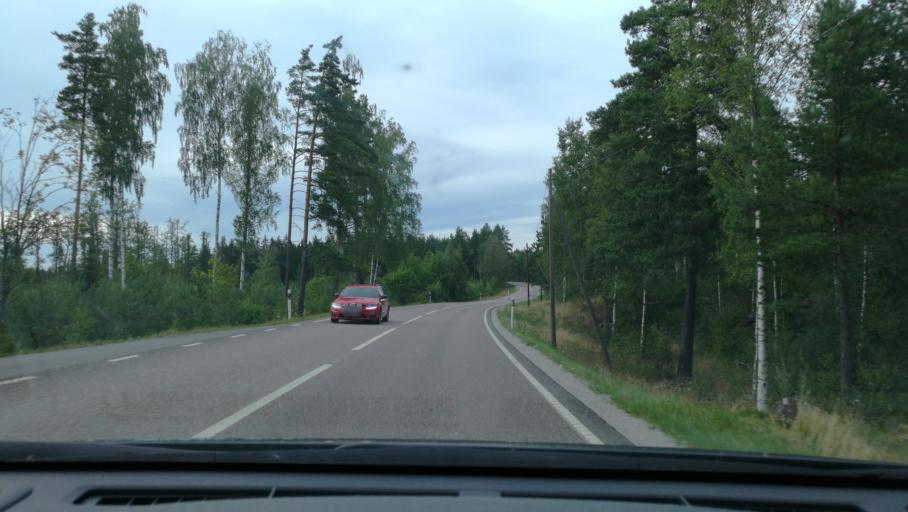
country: SE
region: Vaestmanland
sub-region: Kungsors Kommun
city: Kungsoer
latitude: 59.2915
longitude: 16.1096
